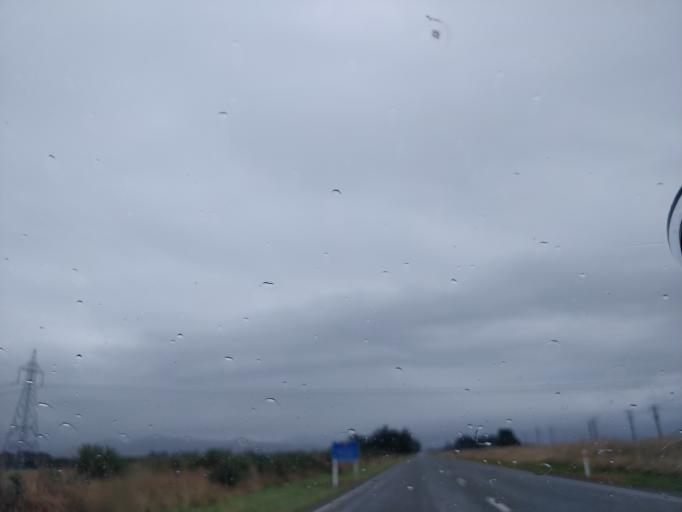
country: NZ
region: Canterbury
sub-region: Selwyn District
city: Darfield
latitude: -43.3841
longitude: 172.0111
